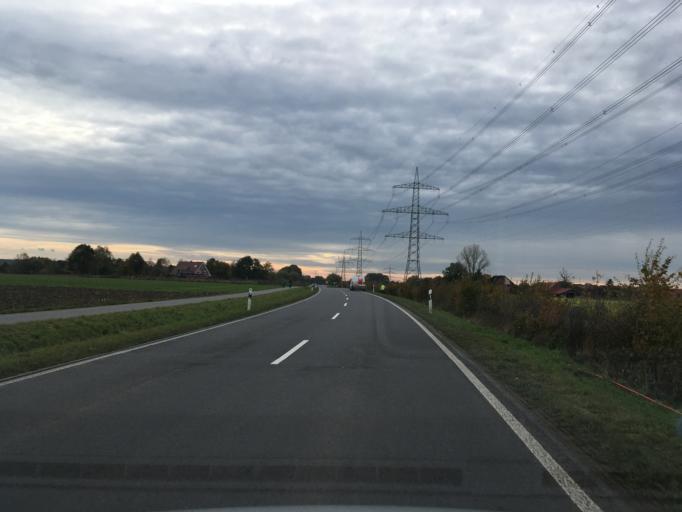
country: DE
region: North Rhine-Westphalia
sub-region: Regierungsbezirk Munster
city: Sudlohn
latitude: 51.8962
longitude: 6.9088
